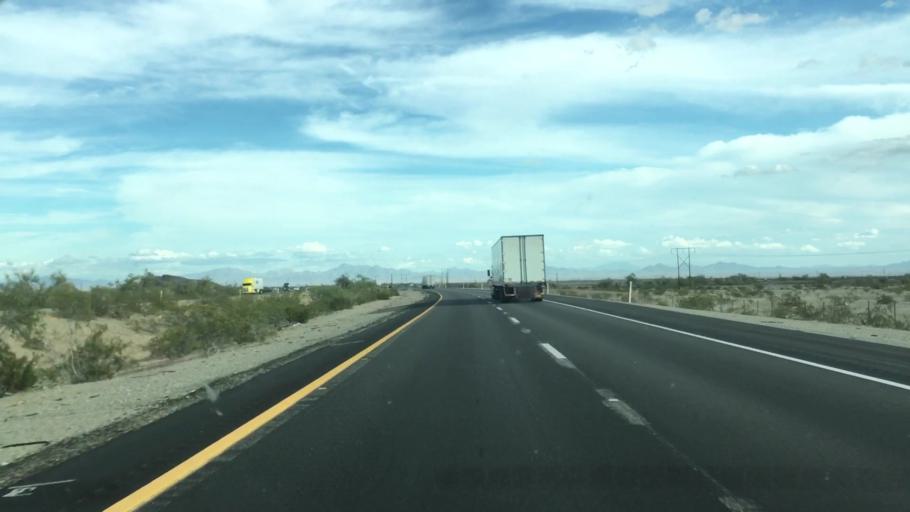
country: US
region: California
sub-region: Riverside County
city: Mesa Verde
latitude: 33.6090
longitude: -114.7742
